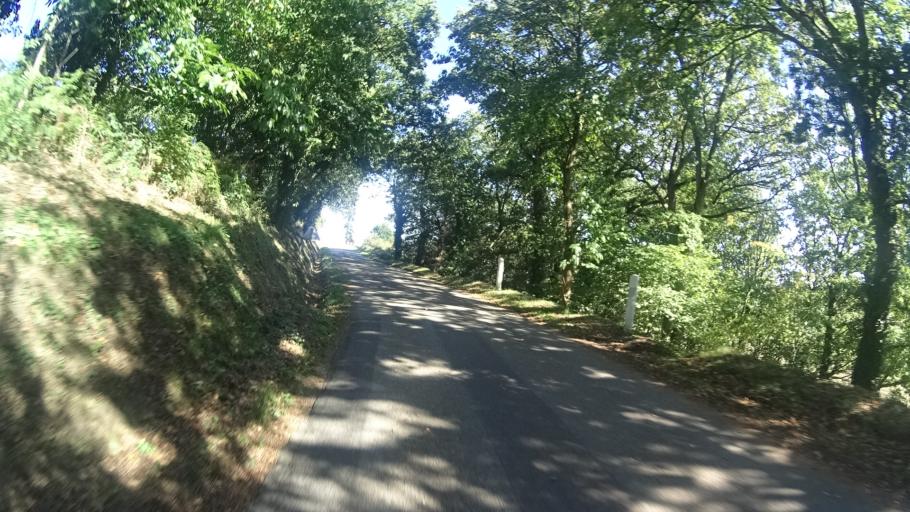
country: FR
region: Brittany
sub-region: Departement du Morbihan
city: Saint-Vincent-sur-Oust
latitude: 47.7249
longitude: -2.1617
